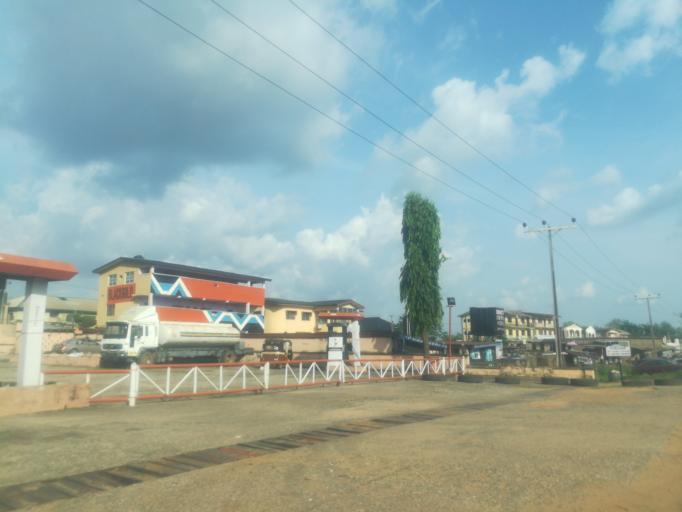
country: NG
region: Oyo
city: Ibadan
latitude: 7.3935
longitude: 3.8128
